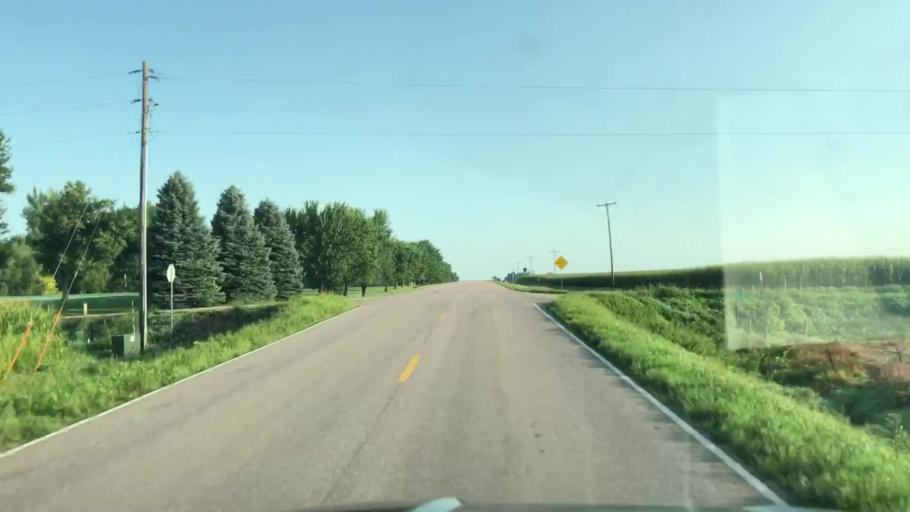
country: US
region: Iowa
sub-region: Lyon County
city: George
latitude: 43.2577
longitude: -96.0001
